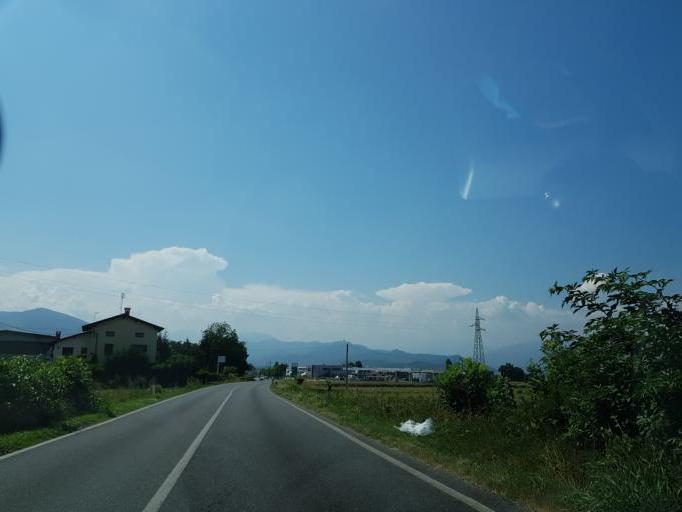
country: IT
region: Piedmont
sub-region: Provincia di Cuneo
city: San Defendente
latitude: 44.3964
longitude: 7.4849
